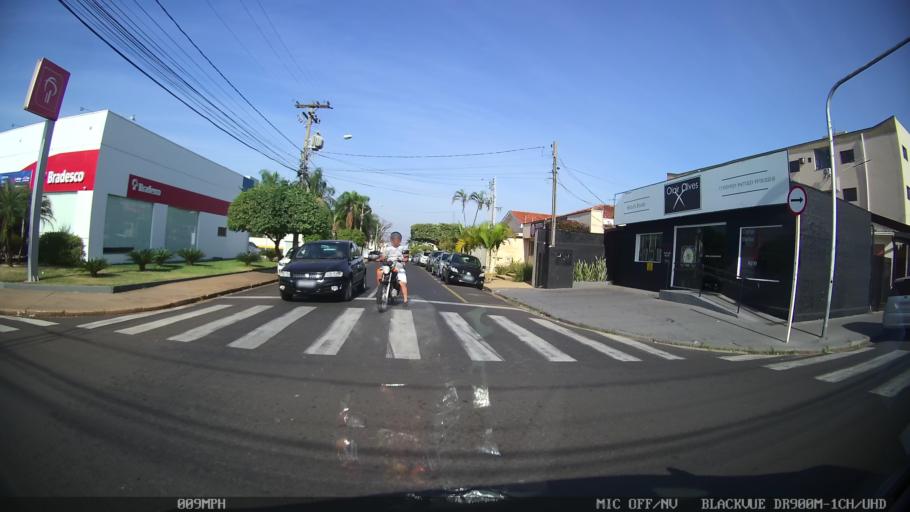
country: BR
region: Sao Paulo
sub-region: Sao Jose Do Rio Preto
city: Sao Jose do Rio Preto
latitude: -20.8026
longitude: -49.3891
